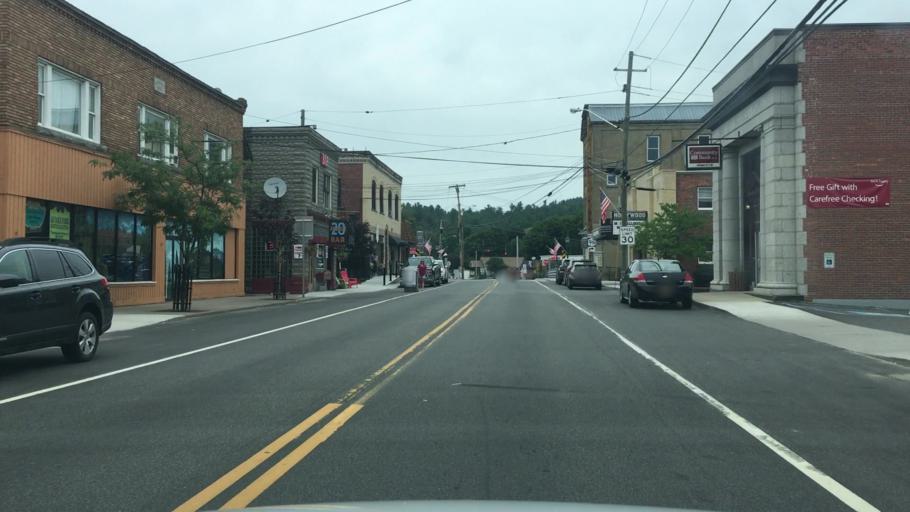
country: US
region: New York
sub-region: Clinton County
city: Peru
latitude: 44.4404
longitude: -73.6764
